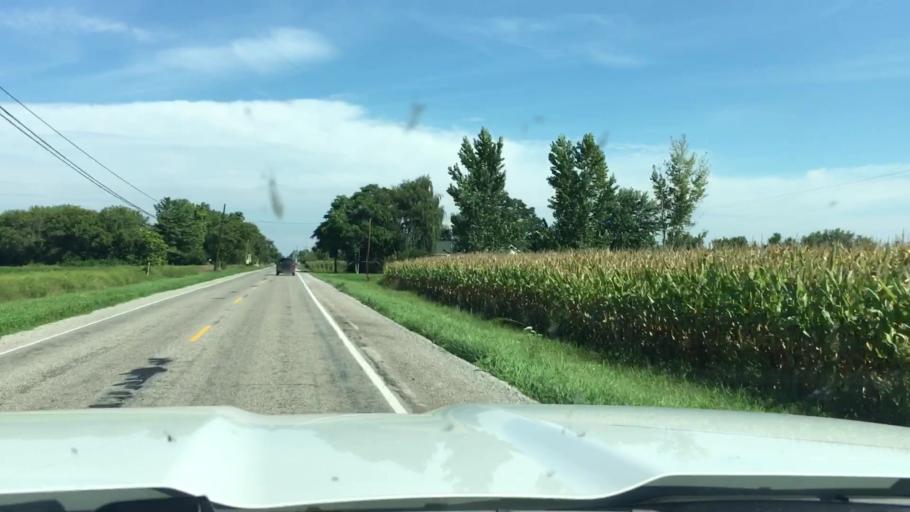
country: US
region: Michigan
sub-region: Saginaw County
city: Hemlock
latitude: 43.4262
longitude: -84.2298
